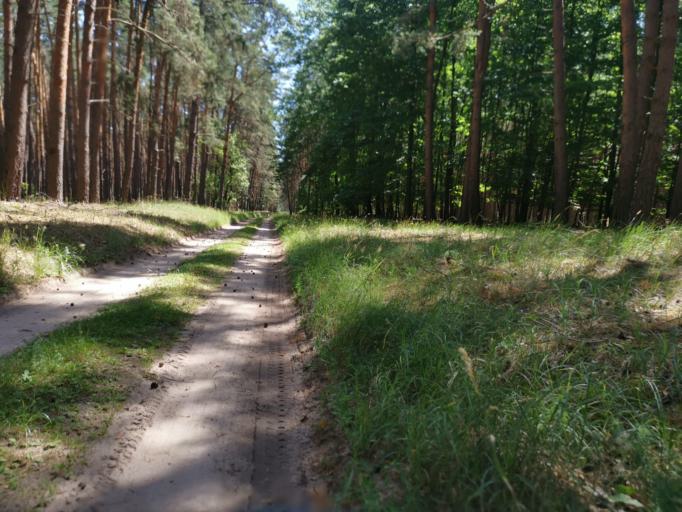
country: CZ
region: South Moravian
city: Vracov
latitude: 48.9584
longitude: 17.2242
